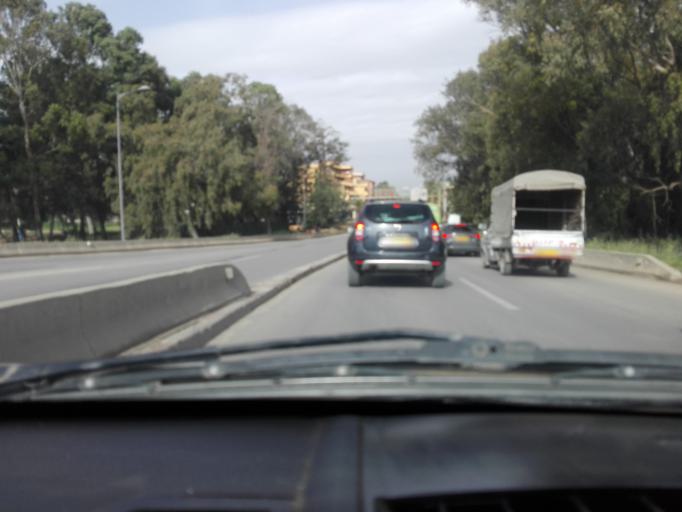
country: DZ
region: Alger
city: Bab Ezzouar
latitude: 36.7254
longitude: 3.1951
